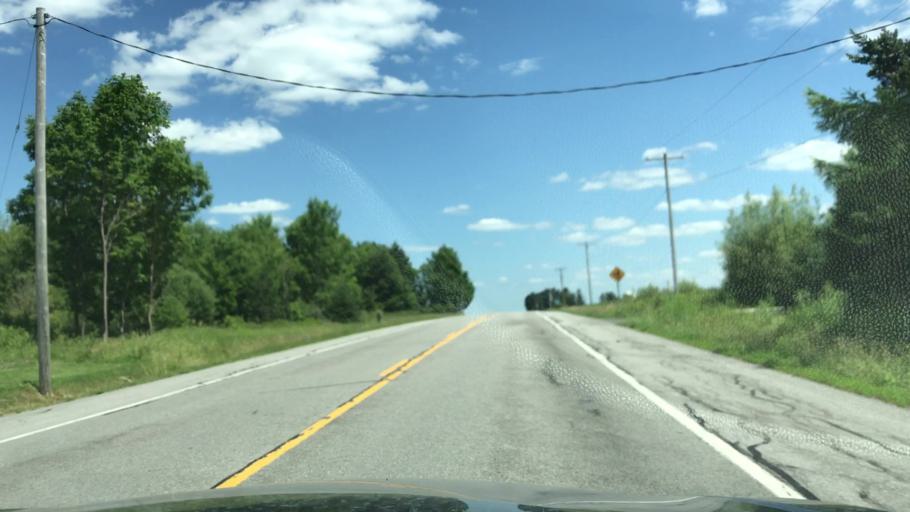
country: US
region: New York
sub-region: Wyoming County
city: Warsaw
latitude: 42.7458
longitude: -78.2229
